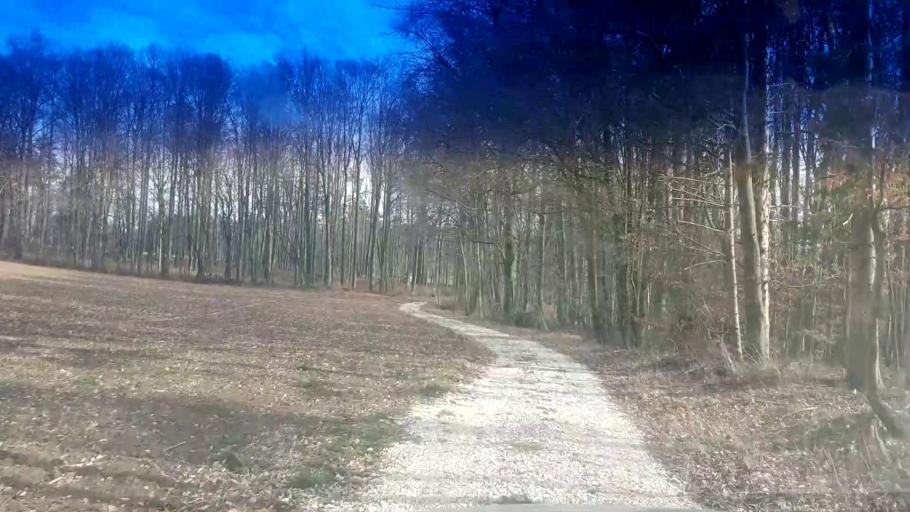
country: DE
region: Bavaria
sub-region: Upper Franconia
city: Litzendorf
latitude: 49.9274
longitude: 11.0634
